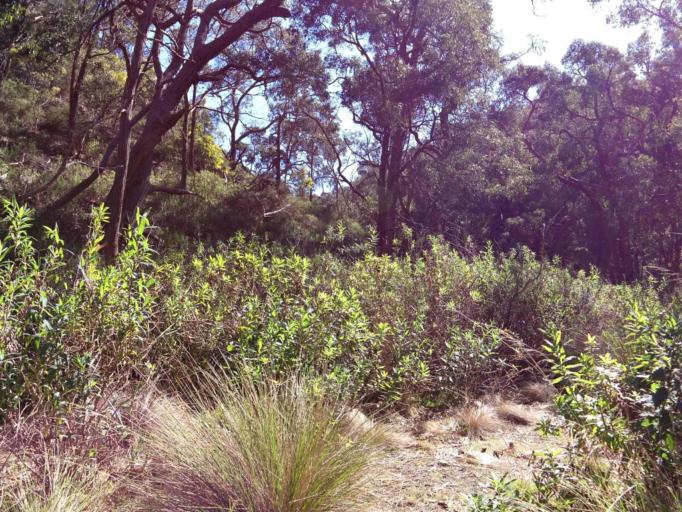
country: AU
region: Victoria
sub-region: Moorabool
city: Bacchus Marsh
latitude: -37.6677
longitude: 144.3183
